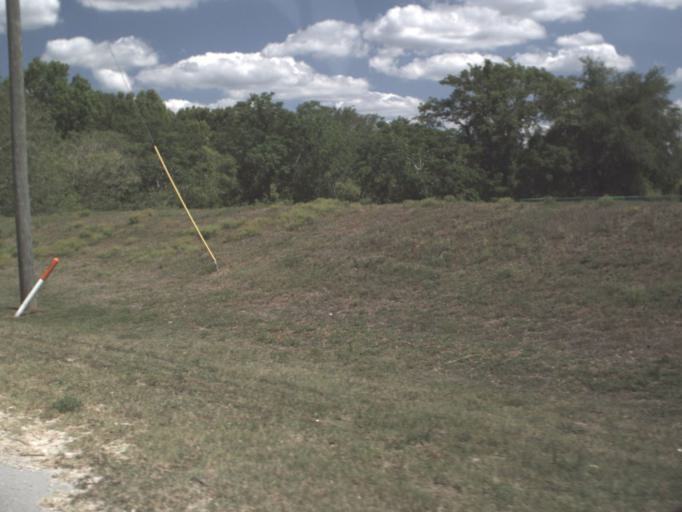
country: US
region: Florida
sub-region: Lake County
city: Mount Dora
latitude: 28.8005
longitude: -81.6110
